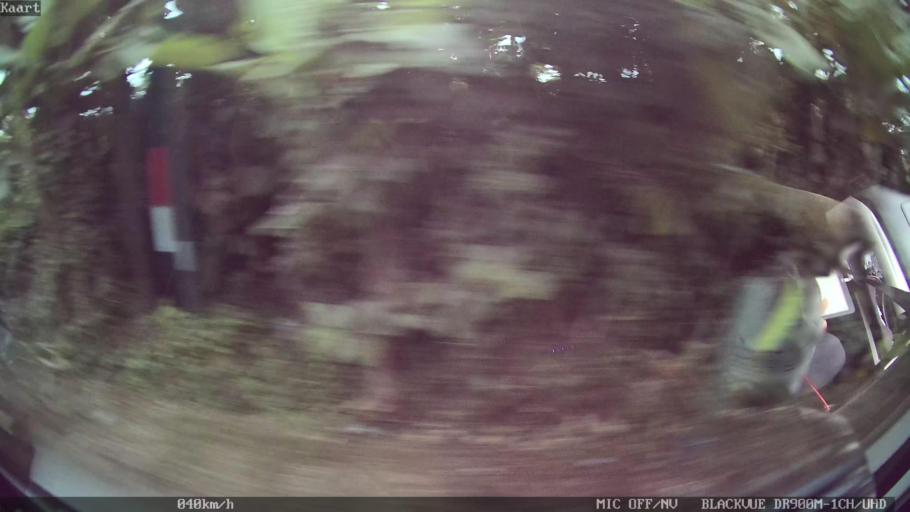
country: ID
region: Bali
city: Banjar Cemenggon
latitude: -8.5426
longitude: 115.2106
